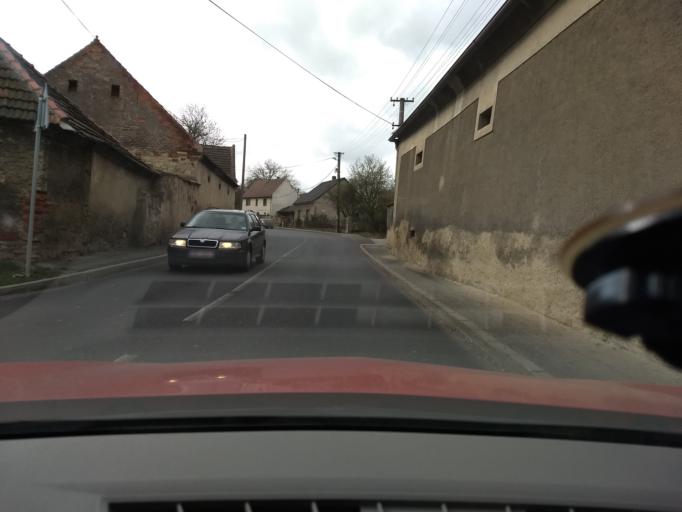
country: CZ
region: Central Bohemia
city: Unhost'
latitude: 50.1093
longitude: 14.1354
